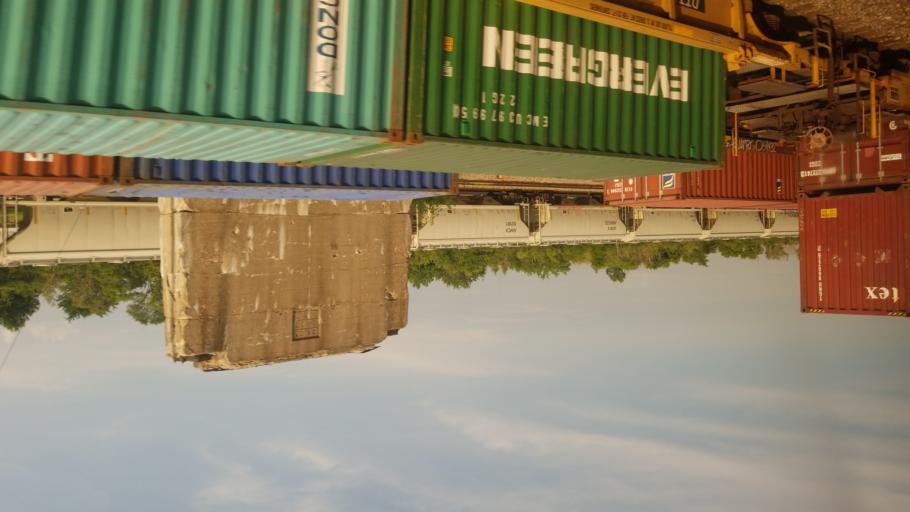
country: US
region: Illinois
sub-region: Kane County
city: Aurora
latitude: 41.7734
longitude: -88.2534
